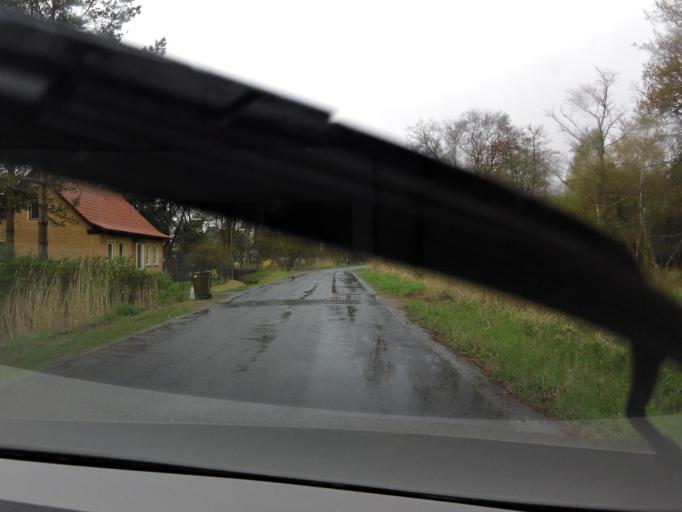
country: DE
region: Mecklenburg-Vorpommern
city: Barth
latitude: 54.4193
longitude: 12.7815
